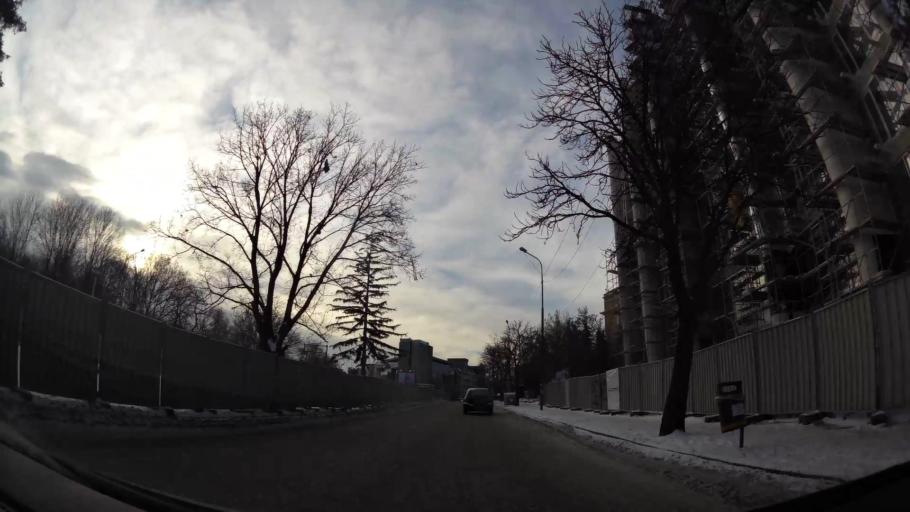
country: BG
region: Sofia-Capital
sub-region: Stolichna Obshtina
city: Sofia
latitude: 42.6758
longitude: 23.3338
